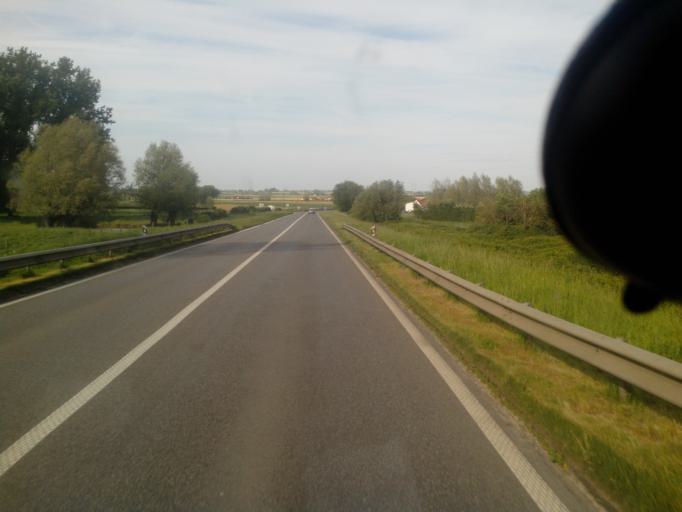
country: FR
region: Nord-Pas-de-Calais
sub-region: Departement du Nord
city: Hazebrouck
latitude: 50.7317
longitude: 2.5176
